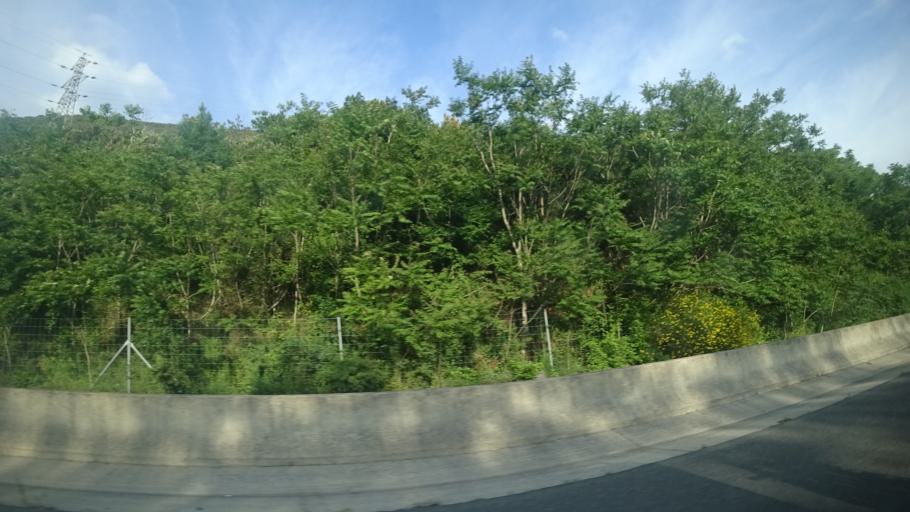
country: FR
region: Languedoc-Roussillon
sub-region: Departement de l'Herault
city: Lodeve
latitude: 43.7158
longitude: 3.3245
